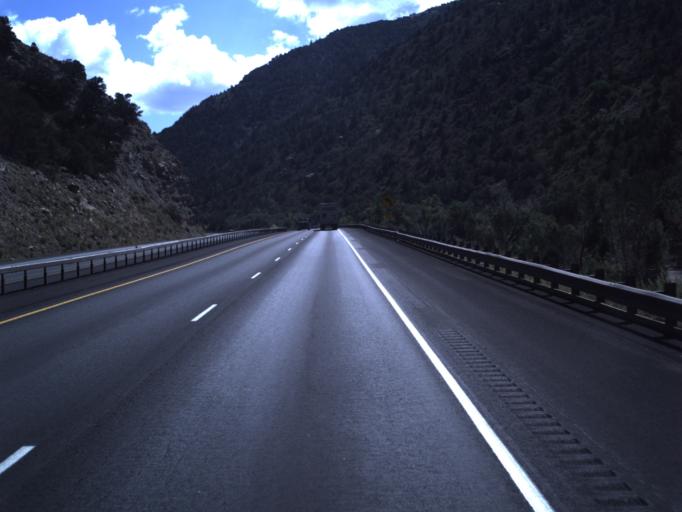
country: US
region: Utah
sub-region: Sevier County
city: Salina
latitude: 38.8978
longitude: -111.6304
